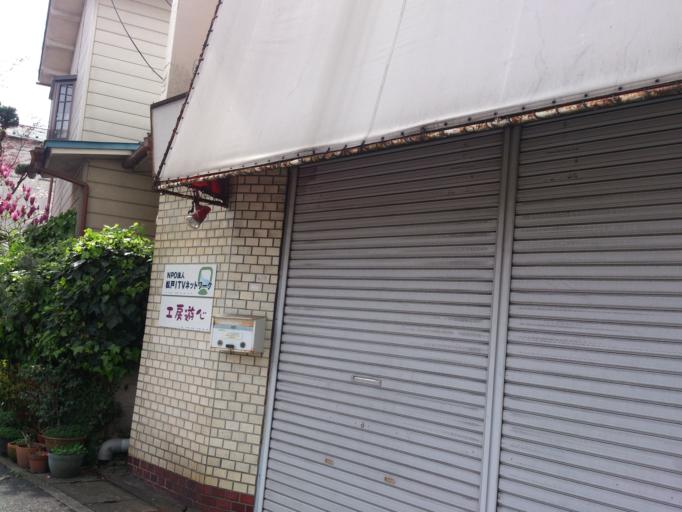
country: JP
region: Chiba
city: Matsudo
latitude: 35.7910
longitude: 139.9031
